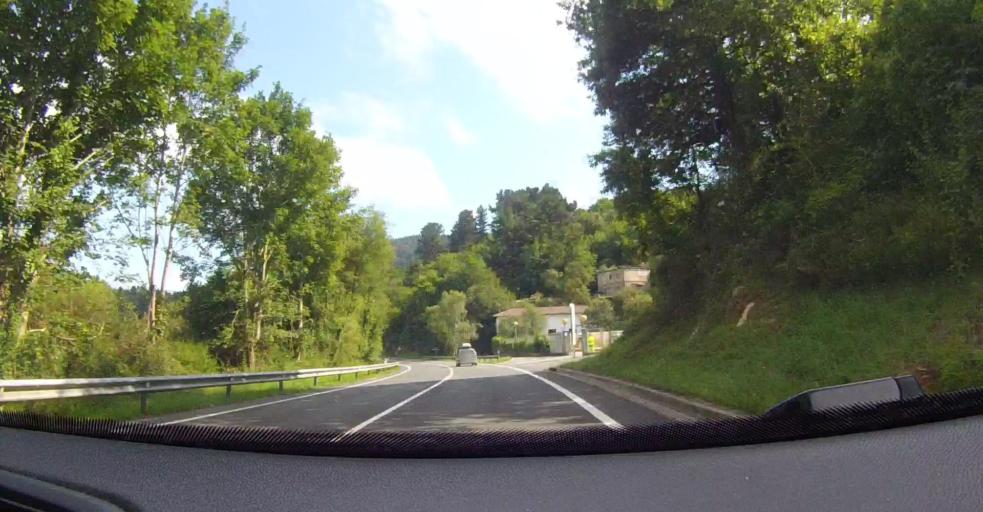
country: ES
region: Basque Country
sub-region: Bizkaia
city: Ibarrangelu
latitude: 43.3635
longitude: -2.6405
